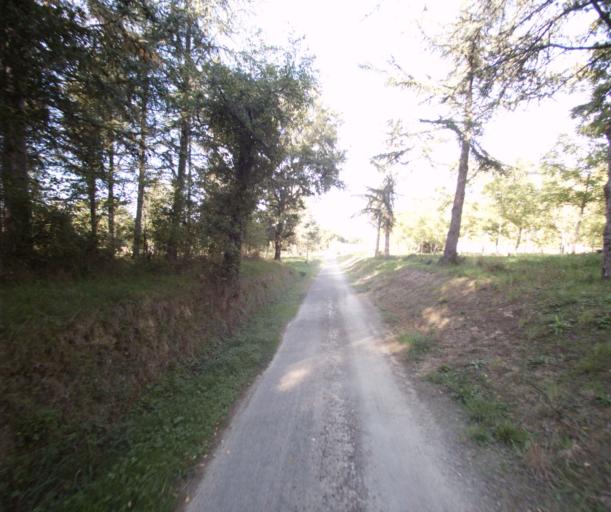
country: FR
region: Midi-Pyrenees
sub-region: Departement du Gers
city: Eauze
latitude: 43.8621
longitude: 0.0243
